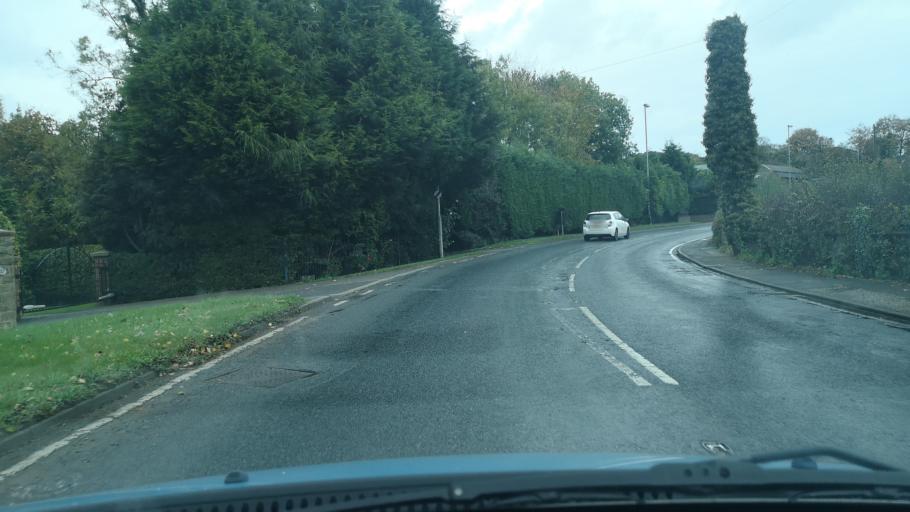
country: GB
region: England
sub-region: City and Borough of Wakefield
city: Hemsworth
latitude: 53.6204
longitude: -1.3463
